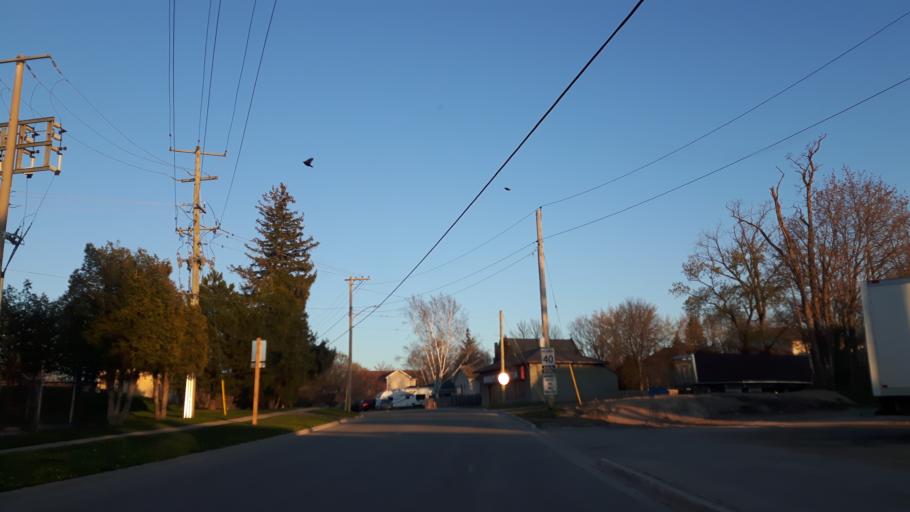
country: CA
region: Ontario
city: Bluewater
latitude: 43.6192
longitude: -81.5391
